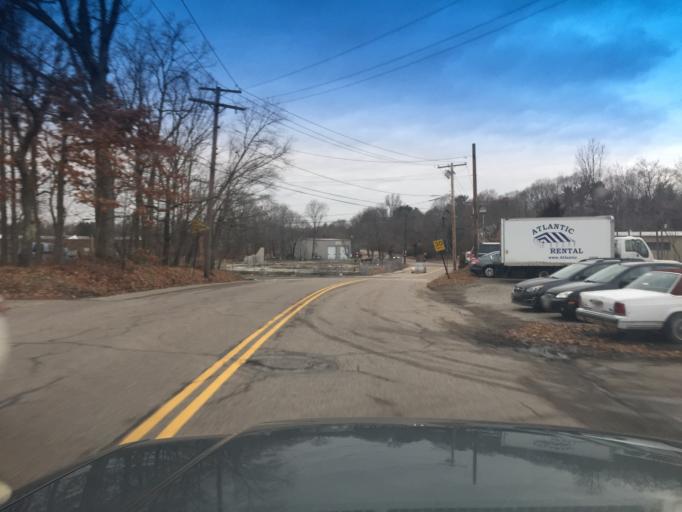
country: US
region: Massachusetts
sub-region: Norfolk County
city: Millis-Clicquot
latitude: 42.1720
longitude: -71.3508
